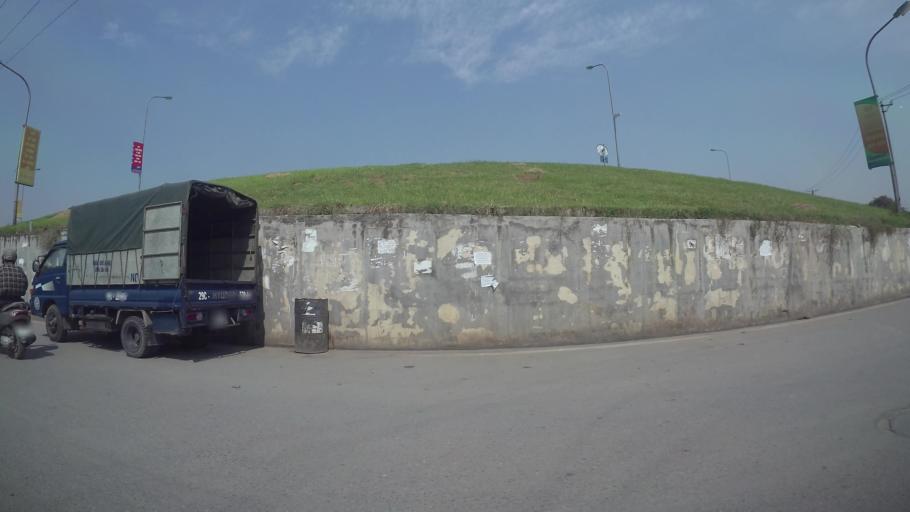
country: VN
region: Ha Noi
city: Hoan Kiem
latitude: 21.0560
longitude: 105.8663
